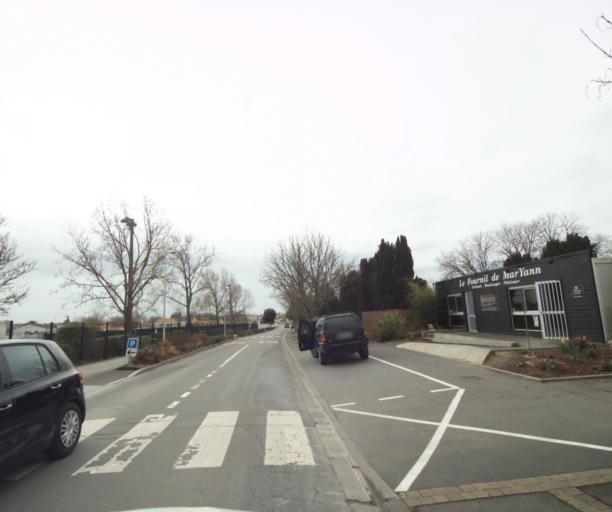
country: FR
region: Poitou-Charentes
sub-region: Departement de la Charente-Maritime
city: Lagord
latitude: 46.1913
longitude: -1.1569
